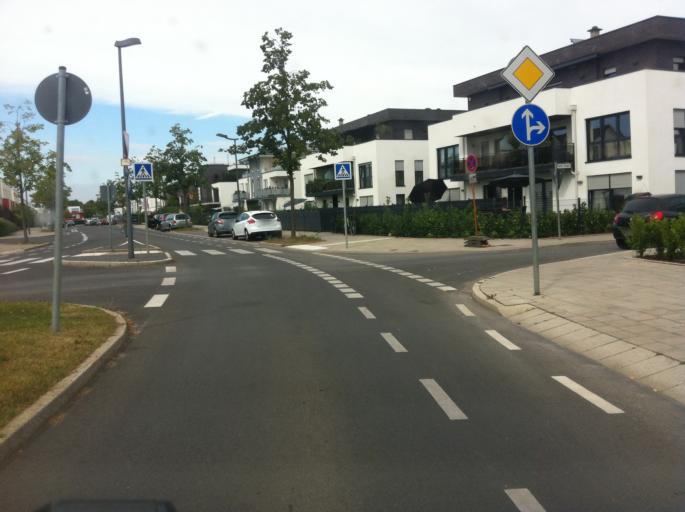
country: DE
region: North Rhine-Westphalia
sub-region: Regierungsbezirk Koln
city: Mengenich
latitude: 50.9644
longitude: 6.8430
